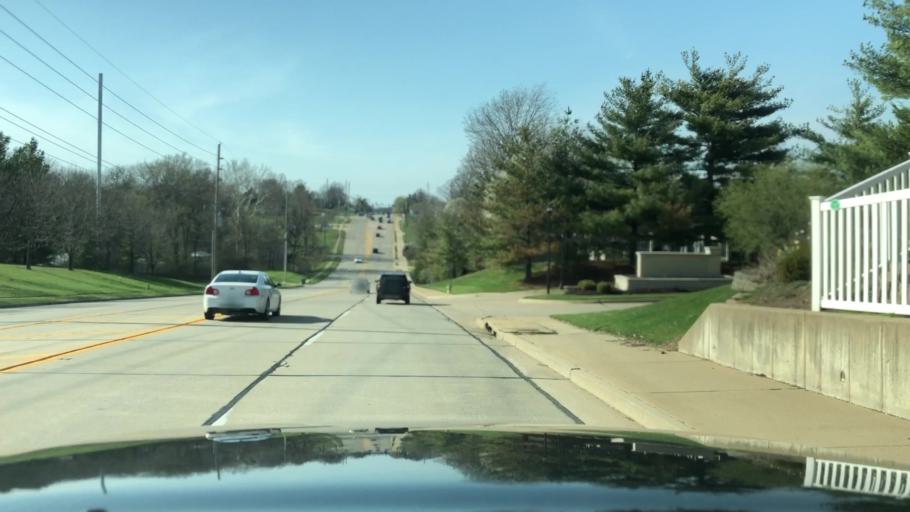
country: US
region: Missouri
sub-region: Saint Charles County
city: Saint Charles
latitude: 38.7694
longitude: -90.5472
